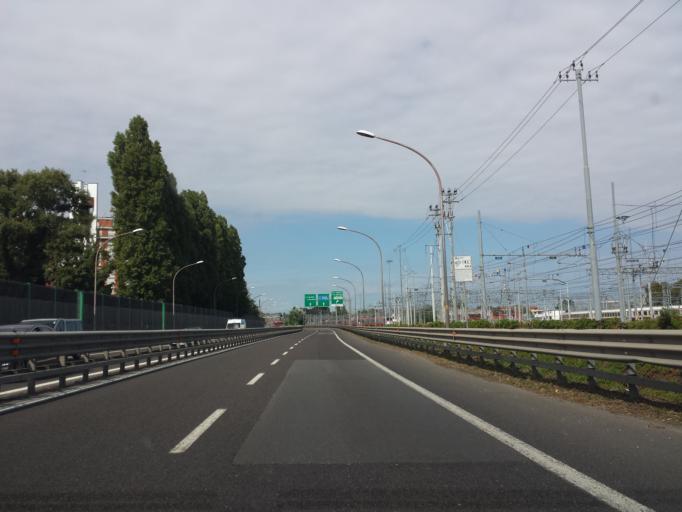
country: IT
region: Veneto
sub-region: Provincia di Venezia
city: Mestre
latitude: 45.4820
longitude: 12.2284
